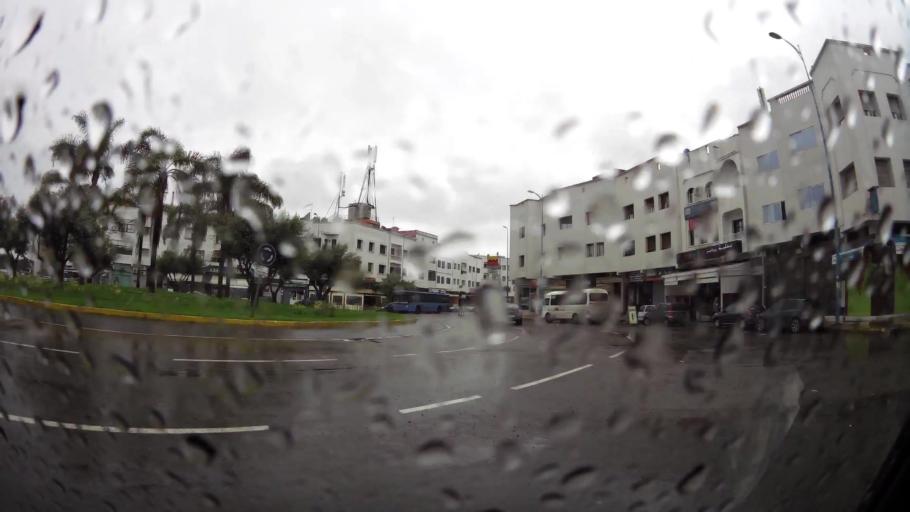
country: MA
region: Grand Casablanca
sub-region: Casablanca
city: Casablanca
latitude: 33.5472
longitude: -7.6816
